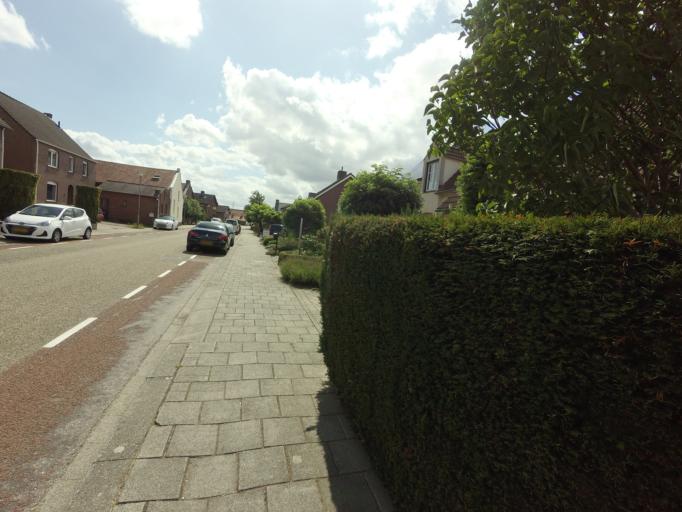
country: NL
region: Limburg
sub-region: Gemeente Maasgouw
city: Maasbracht
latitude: 51.1346
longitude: 5.8609
